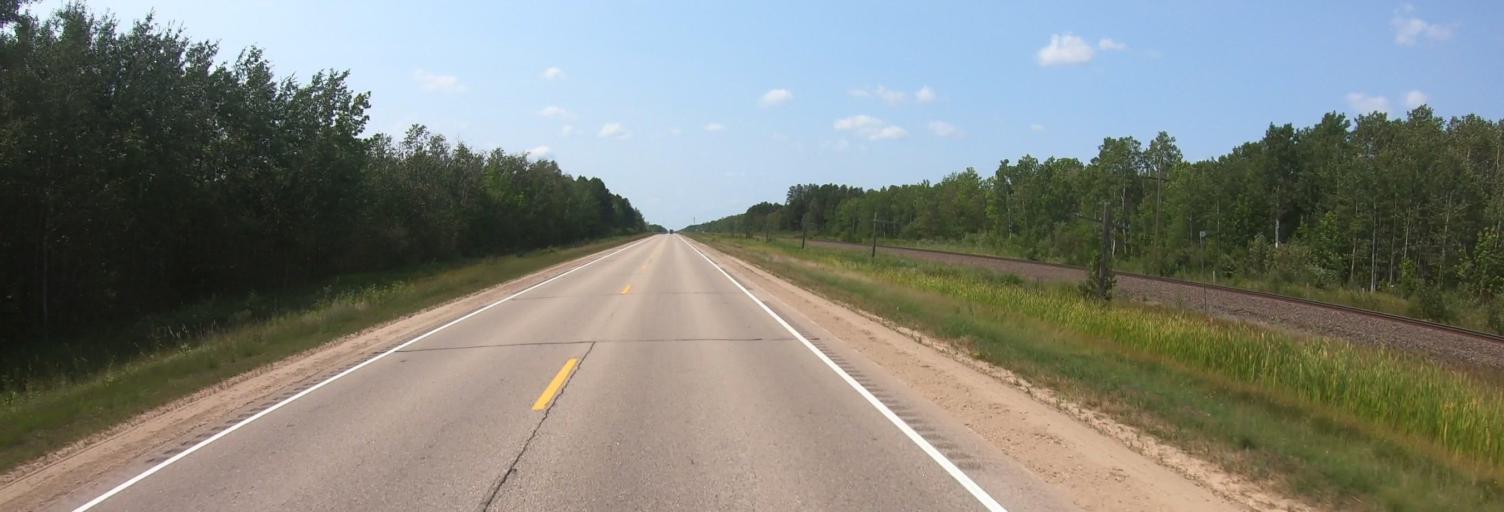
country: US
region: Minnesota
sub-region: Roseau County
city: Warroad
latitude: 48.7746
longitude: -94.9858
